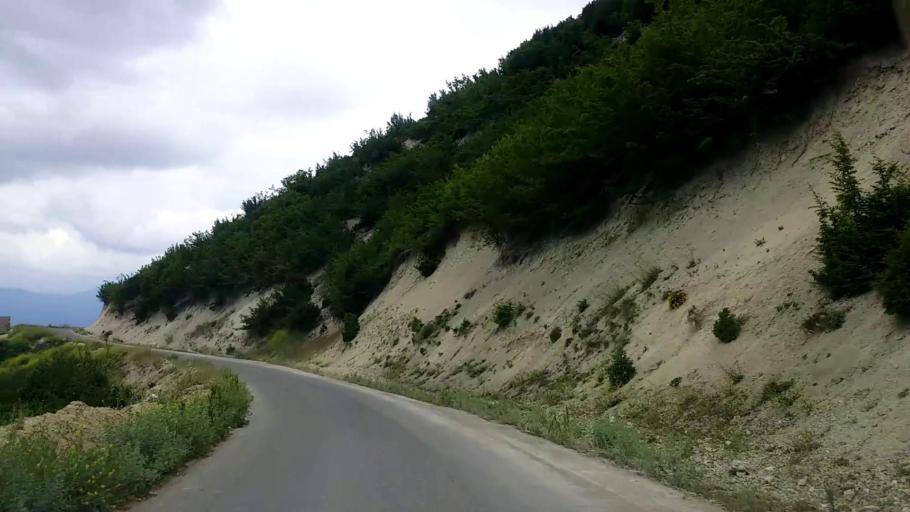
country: IR
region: Mazandaran
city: Chalus
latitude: 36.5413
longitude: 51.2723
